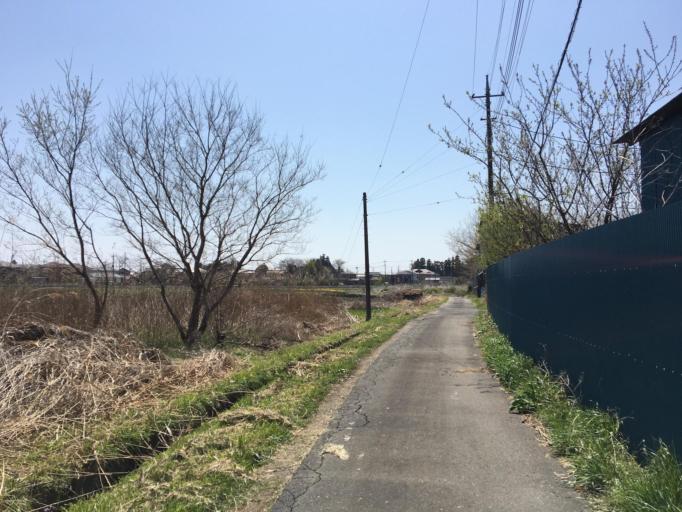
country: JP
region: Saitama
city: Sakado
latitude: 35.9480
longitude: 139.3484
